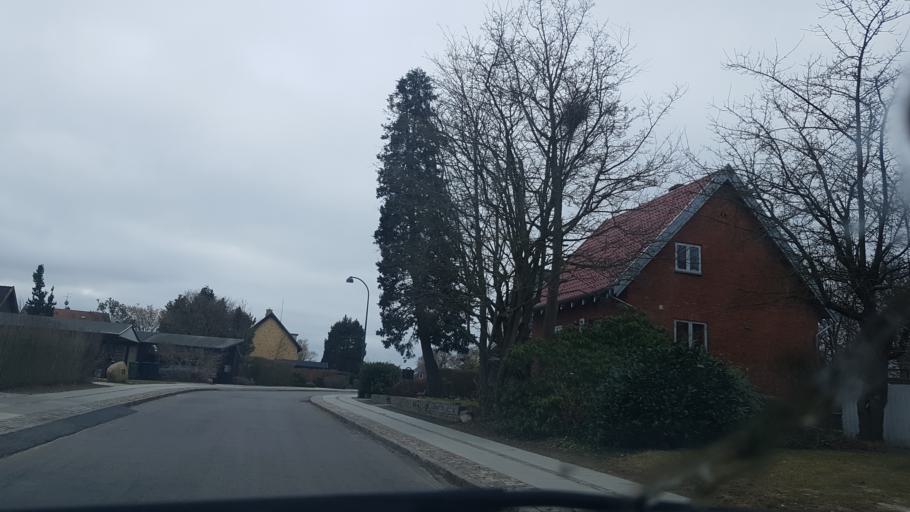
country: DK
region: Capital Region
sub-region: Gladsaxe Municipality
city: Buddinge
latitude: 55.7512
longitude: 12.5013
